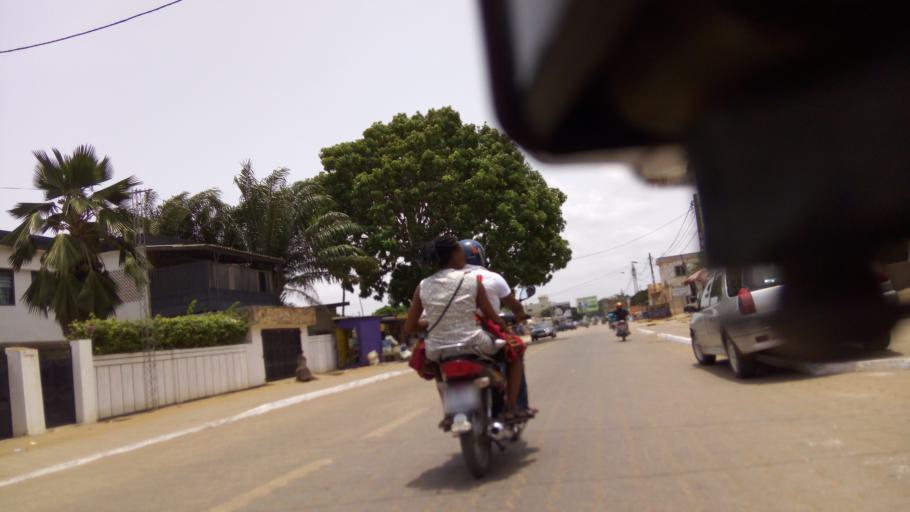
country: TG
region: Maritime
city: Lome
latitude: 6.1553
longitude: 1.2167
